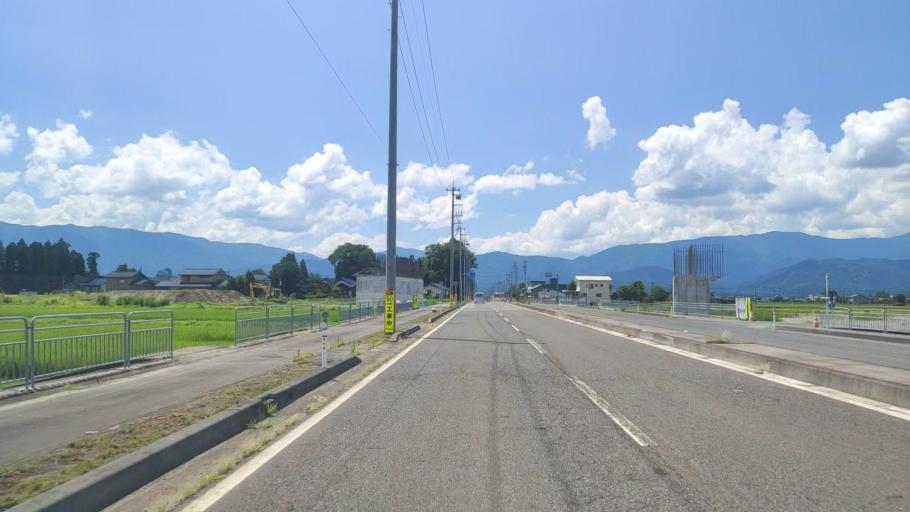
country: JP
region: Fukui
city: Ono
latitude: 35.9987
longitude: 136.5091
